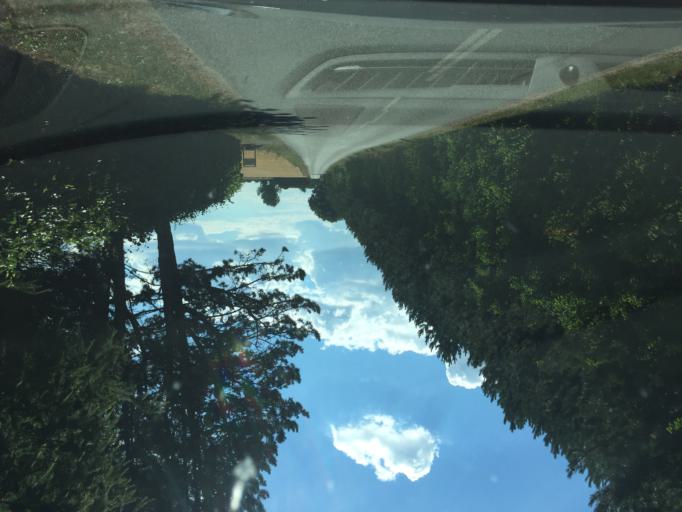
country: DK
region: South Denmark
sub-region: Odense Kommune
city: Bellinge
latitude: 55.2828
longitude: 10.3330
